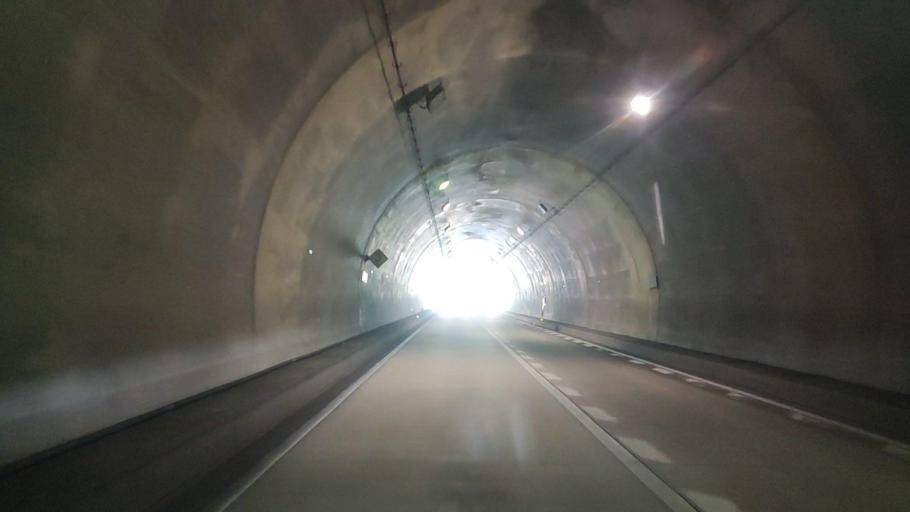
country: JP
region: Nara
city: Yoshino-cho
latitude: 34.2135
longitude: 135.9987
